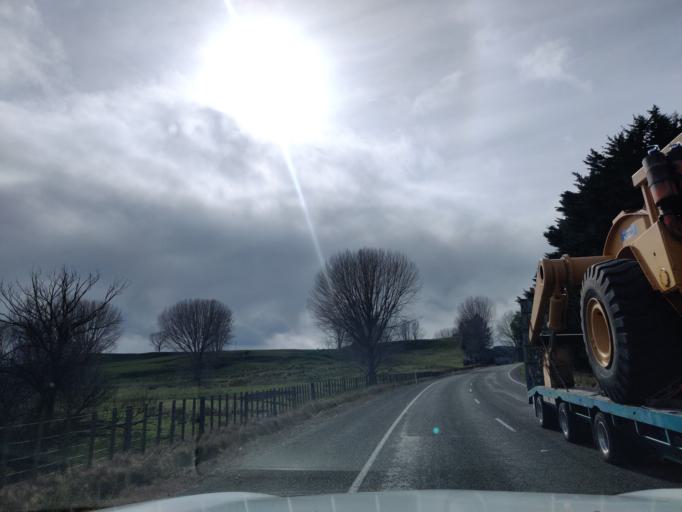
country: NZ
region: Manawatu-Wanganui
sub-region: Ruapehu District
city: Waiouru
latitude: -39.7424
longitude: 175.8361
